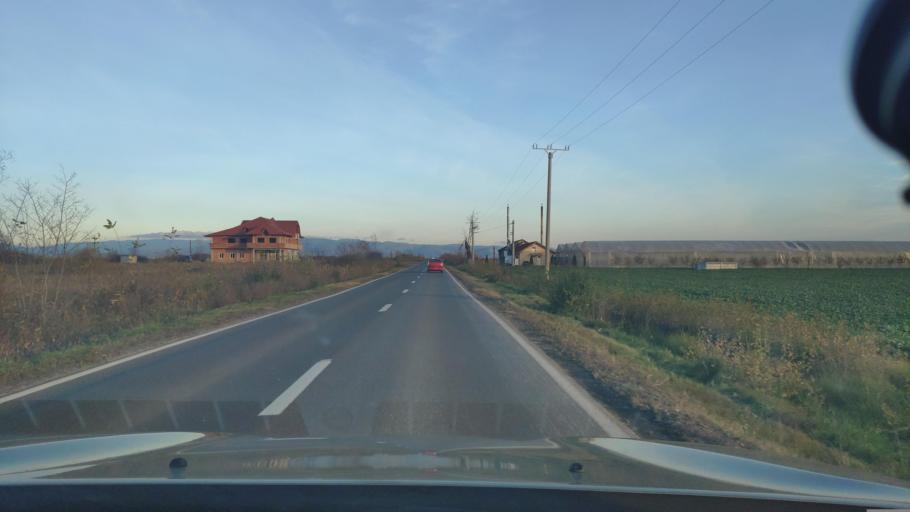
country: RO
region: Satu Mare
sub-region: Comuna Mediesu Aurit
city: Potau
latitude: 47.7728
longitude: 23.1266
